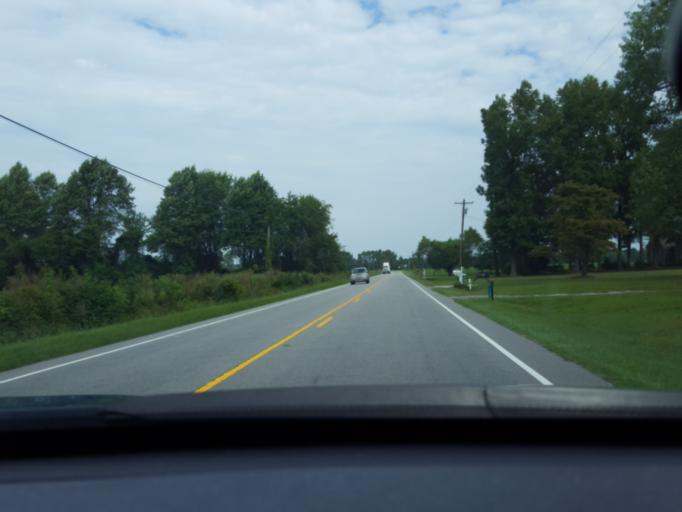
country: US
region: North Carolina
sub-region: Chowan County
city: Edenton
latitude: 36.1532
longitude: -76.6535
